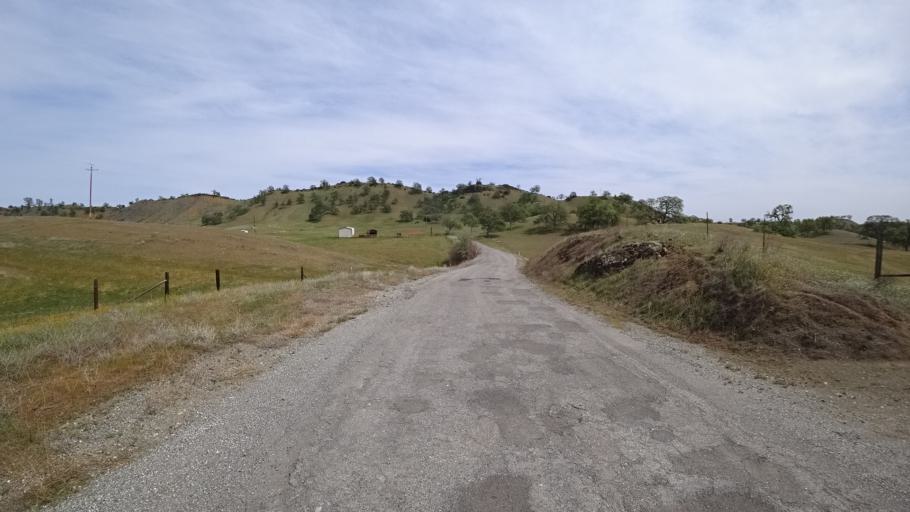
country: US
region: California
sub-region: Glenn County
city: Willows
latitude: 39.6163
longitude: -122.5882
